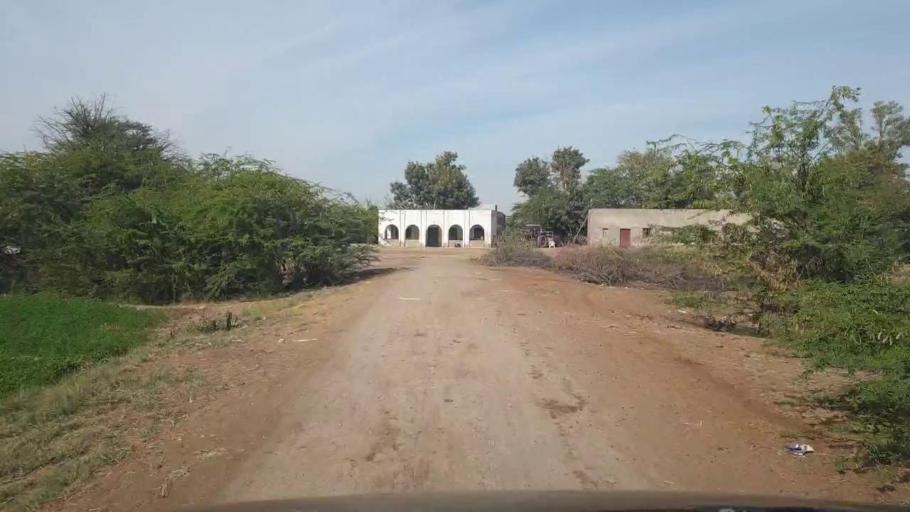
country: PK
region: Sindh
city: Umarkot
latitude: 25.3628
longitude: 69.6959
